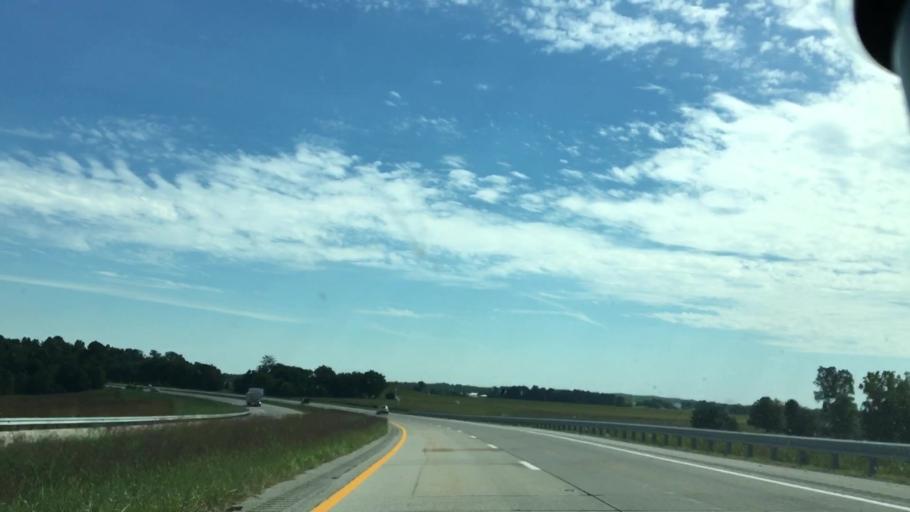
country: US
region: Kentucky
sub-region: Daviess County
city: Owensboro
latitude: 37.7541
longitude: -87.2943
